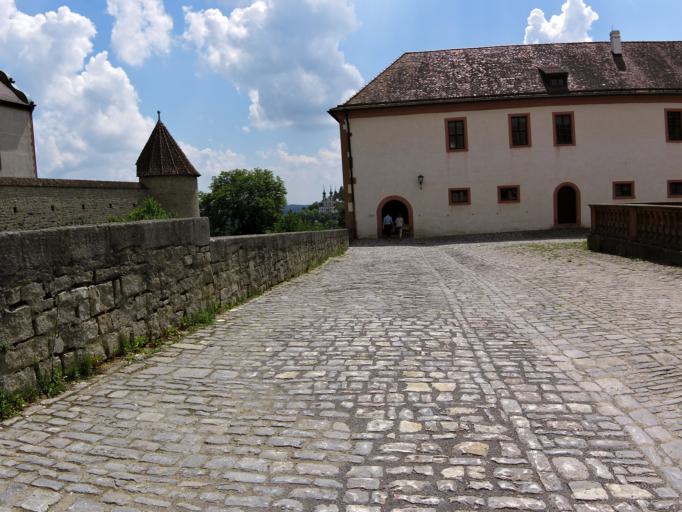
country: DE
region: Bavaria
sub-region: Regierungsbezirk Unterfranken
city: Wuerzburg
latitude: 49.7897
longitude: 9.9195
